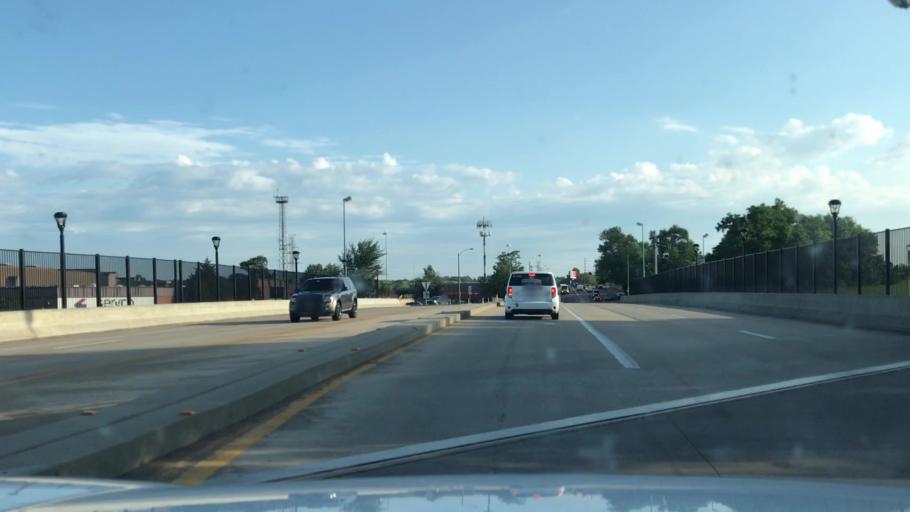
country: US
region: Missouri
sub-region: Saint Louis County
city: Maplewood
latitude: 38.6056
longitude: -90.3073
